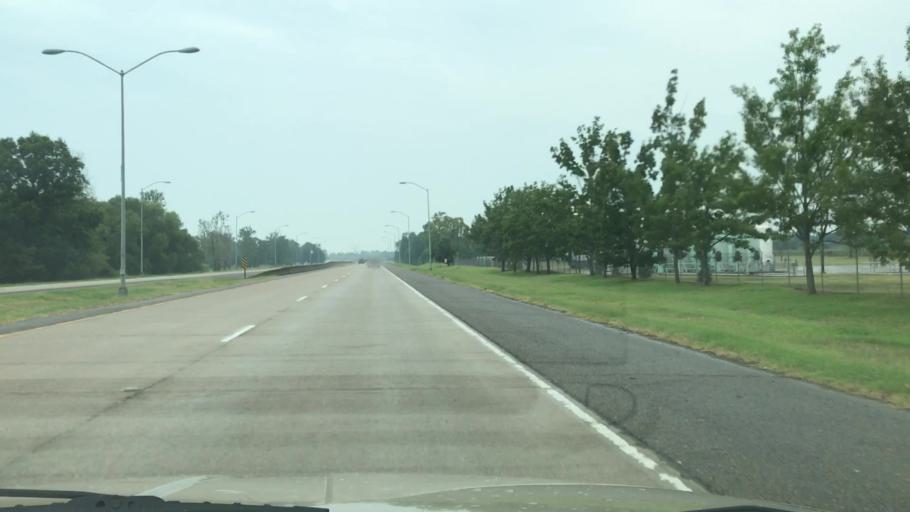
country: US
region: Louisiana
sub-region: Bossier Parish
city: Bossier City
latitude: 32.4819
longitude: -93.6837
